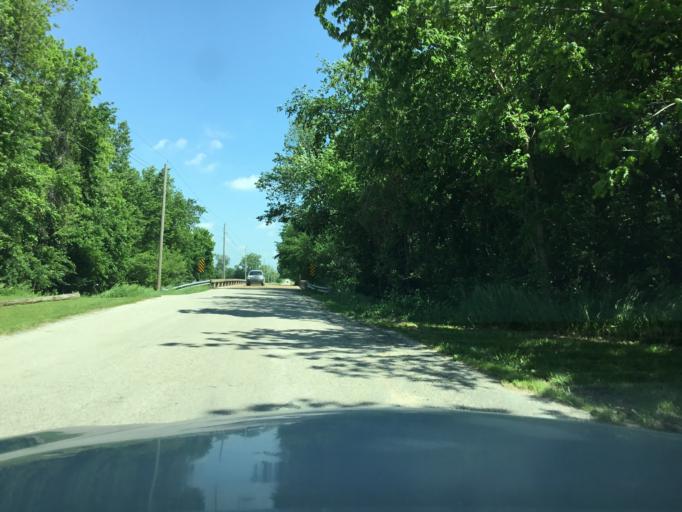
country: US
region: Kansas
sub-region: Labette County
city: Parsons
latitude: 37.3481
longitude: -95.2495
